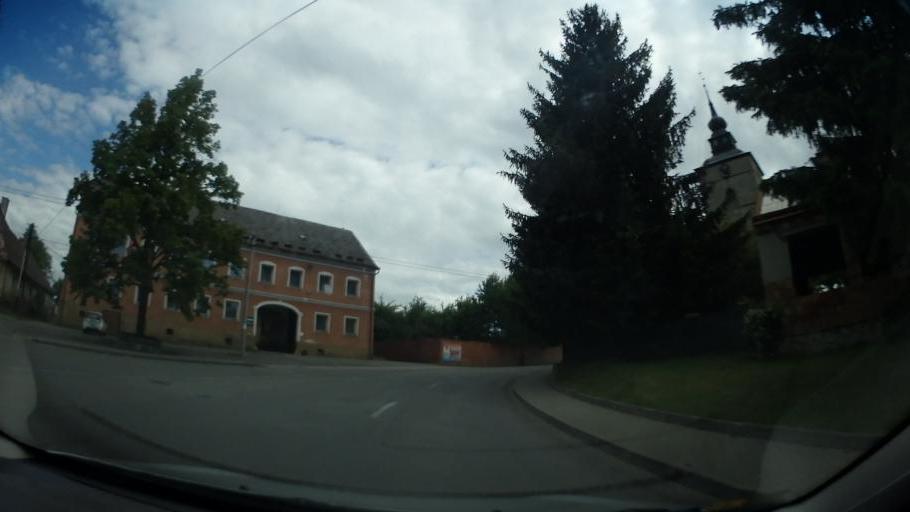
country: CZ
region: Pardubicky
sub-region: Okres Svitavy
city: Moravska Trebova
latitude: 49.7942
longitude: 16.6754
